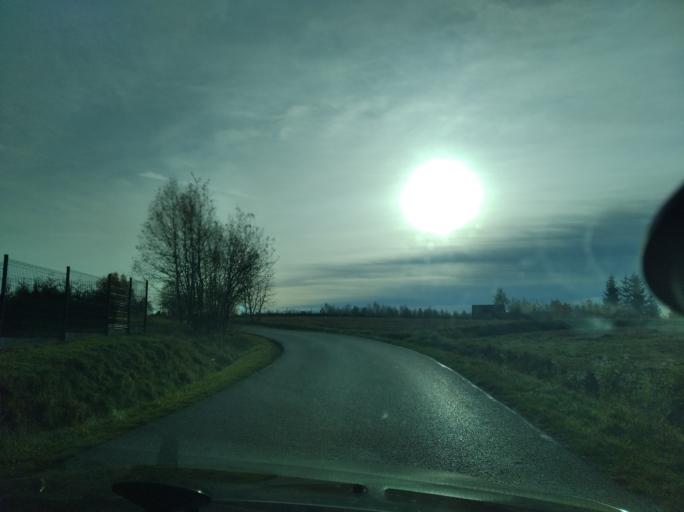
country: PL
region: Subcarpathian Voivodeship
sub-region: Powiat rzeszowski
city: Siedliska
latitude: 49.9348
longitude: 21.9739
